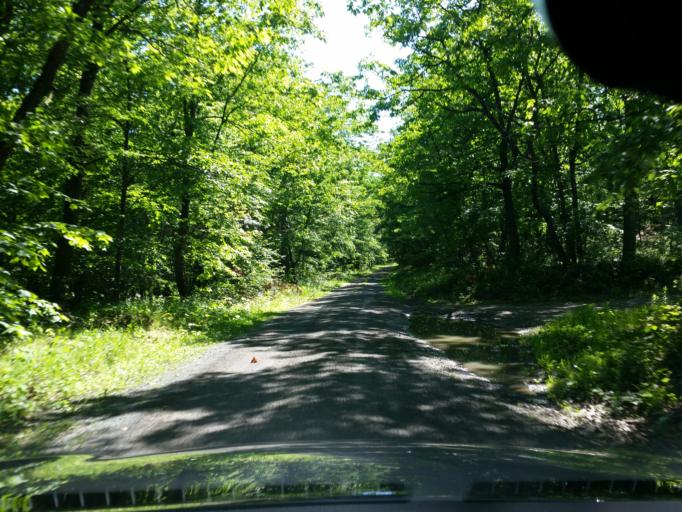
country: US
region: Pennsylvania
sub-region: Lycoming County
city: Duboistown
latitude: 41.1190
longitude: -77.1183
